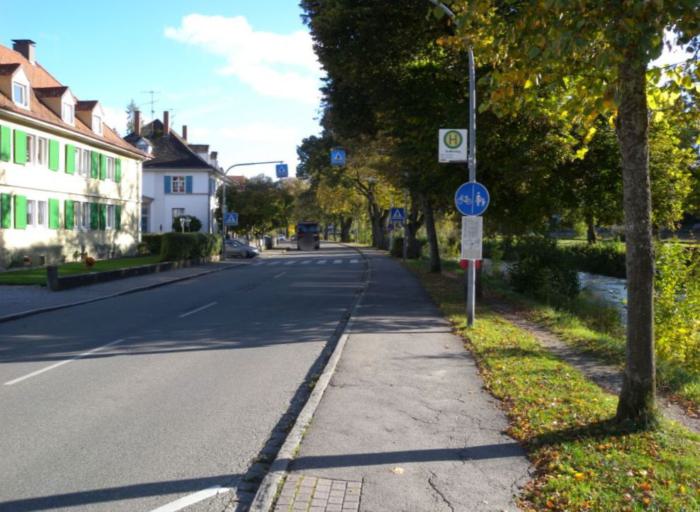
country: DE
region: Baden-Wuerttemberg
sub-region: Freiburg Region
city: Donaueschingen
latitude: 47.9521
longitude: 8.4900
